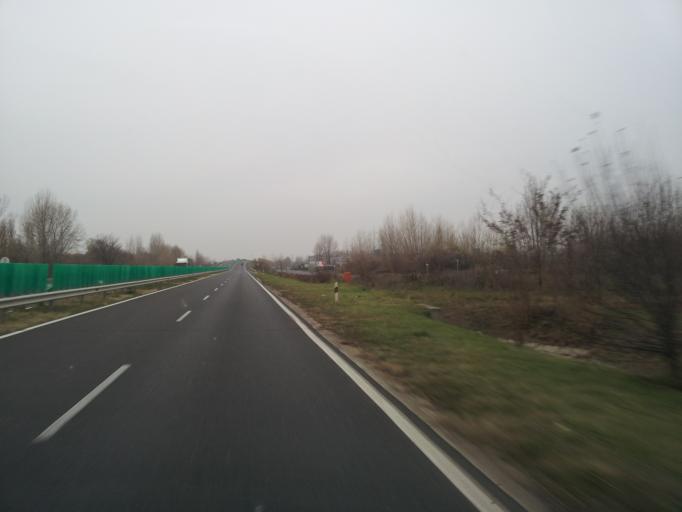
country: HU
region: Fejer
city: Szekesfehervar
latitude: 47.1476
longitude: 18.4162
